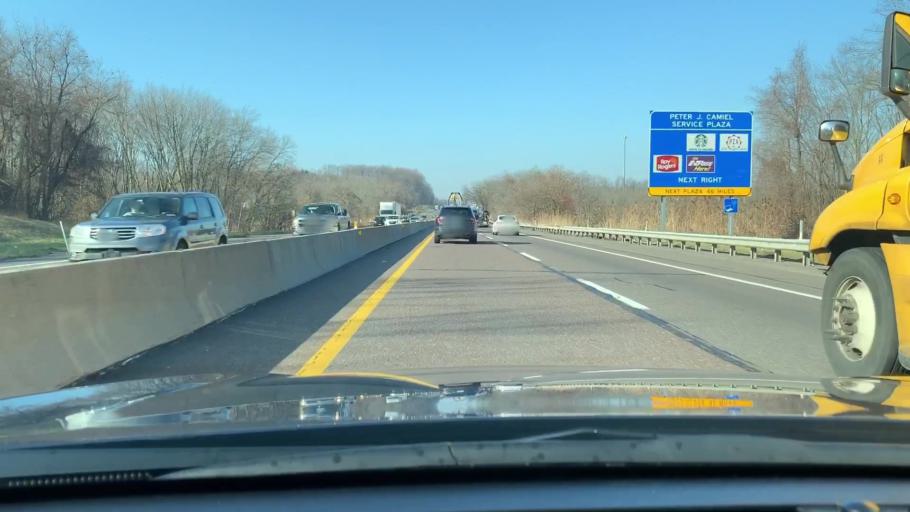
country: US
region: Pennsylvania
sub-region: Chester County
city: Elverson
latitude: 40.1179
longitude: -75.7684
